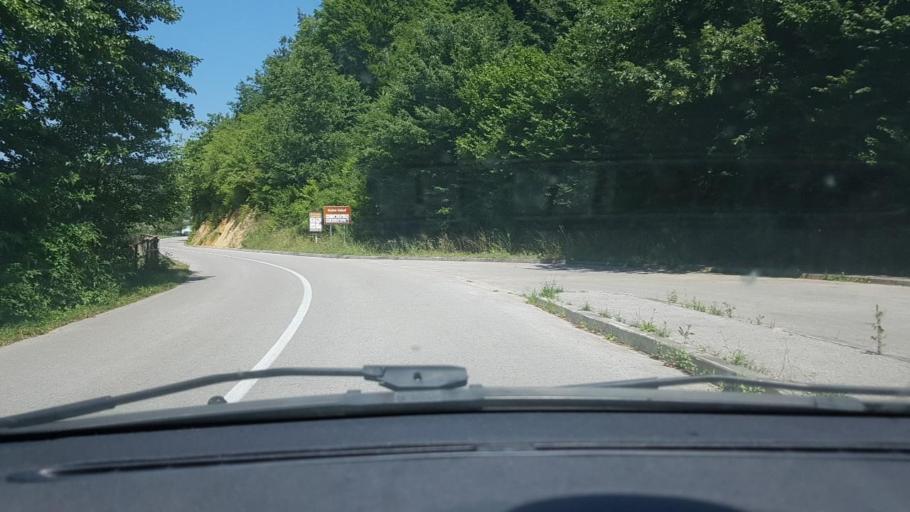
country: BA
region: Federation of Bosnia and Herzegovina
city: Orasac
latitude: 44.5603
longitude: 16.1028
